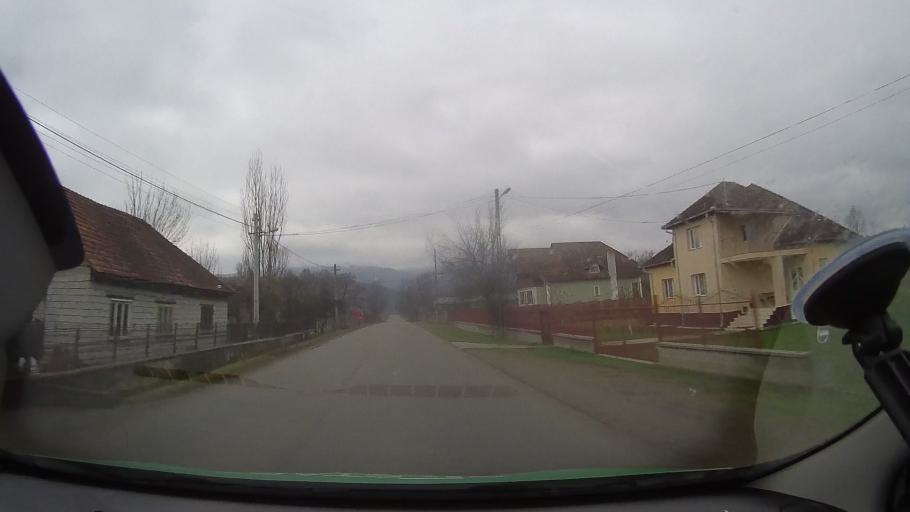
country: RO
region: Hunedoara
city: Vata de Jos
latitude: 46.1884
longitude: 22.6067
